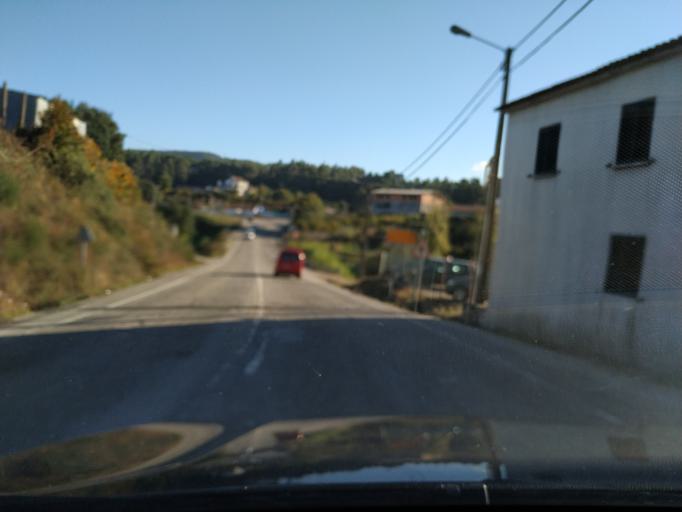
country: PT
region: Aveiro
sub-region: Vale de Cambra
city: Vale de Cambra
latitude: 40.8797
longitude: -8.4251
